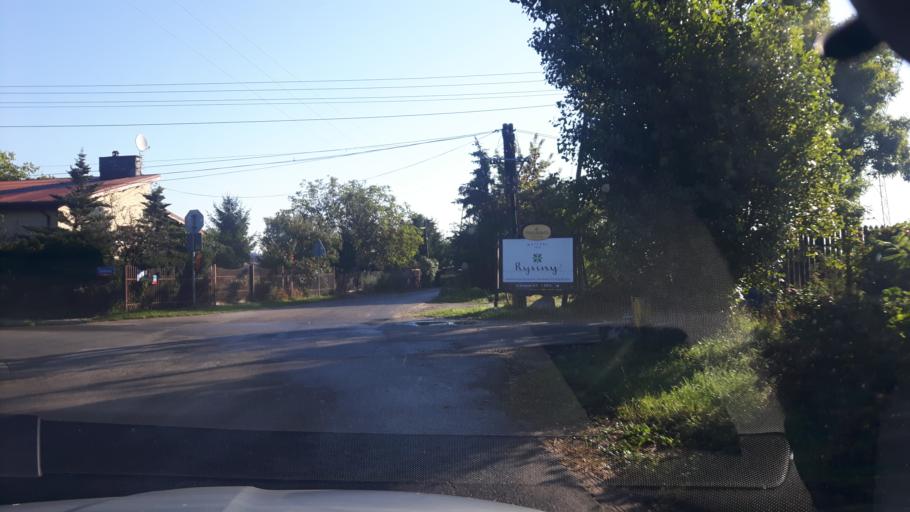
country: PL
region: Masovian Voivodeship
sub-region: Warszawa
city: Bialoleka
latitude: 52.3246
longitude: 21.0021
